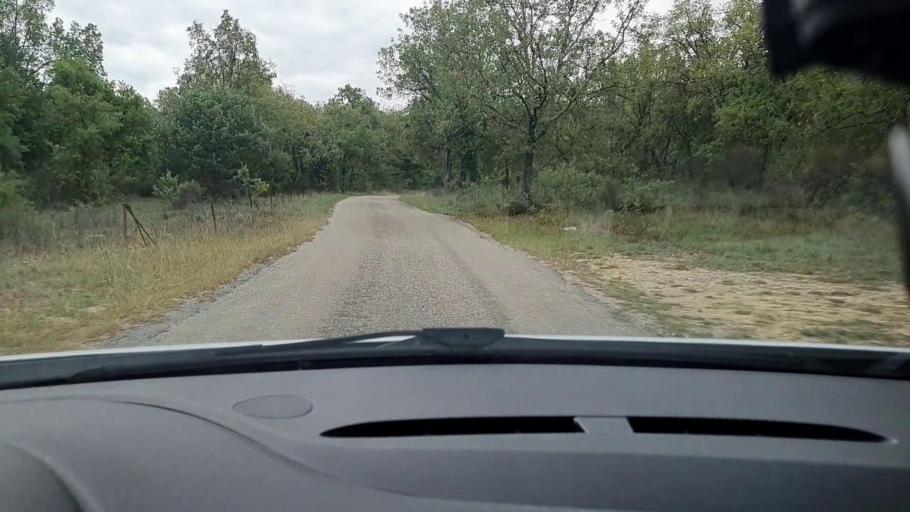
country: FR
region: Languedoc-Roussillon
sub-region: Departement du Gard
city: Mons
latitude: 44.1554
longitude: 4.2905
